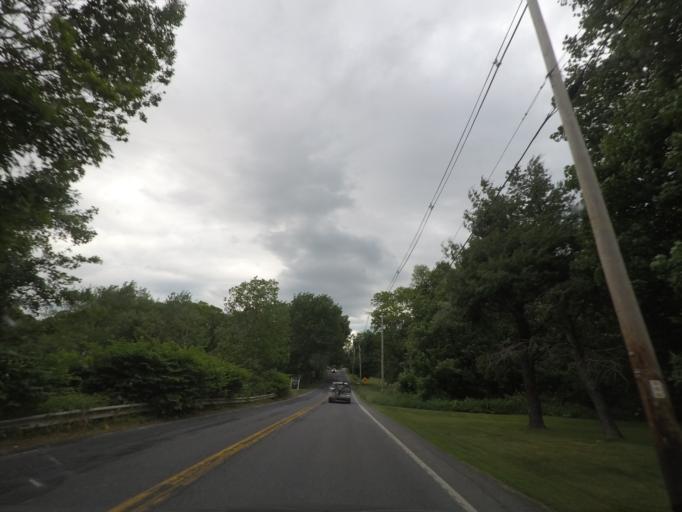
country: US
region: New York
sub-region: Dutchess County
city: Pine Plains
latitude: 41.9765
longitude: -73.5822
